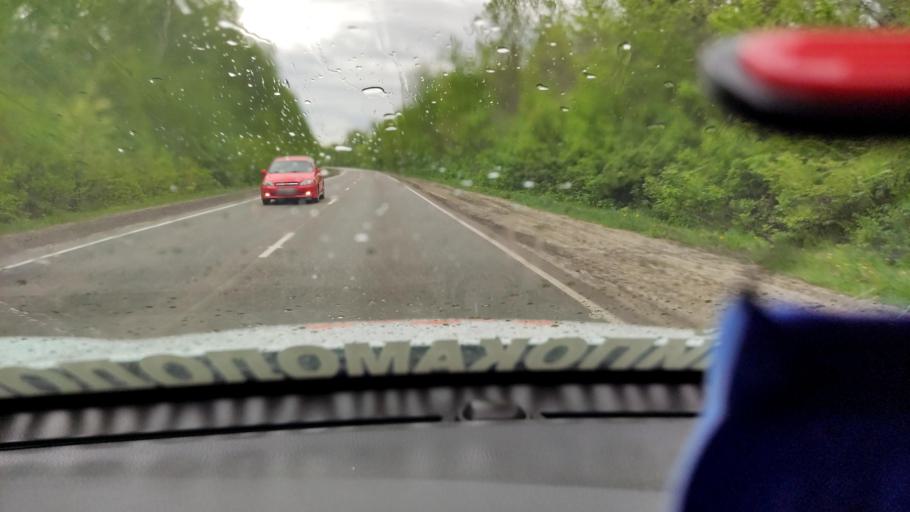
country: RU
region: Voronezj
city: Imeni Pervogo Maya
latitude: 50.7469
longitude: 39.3870
